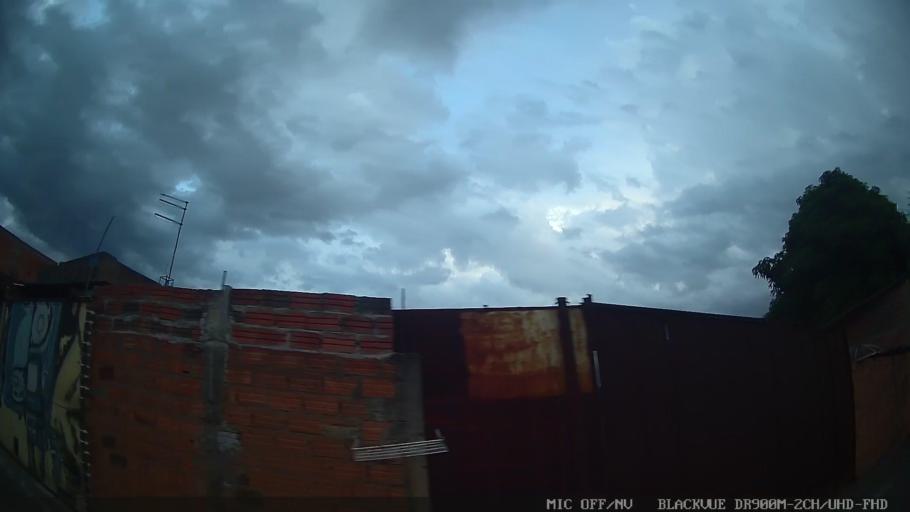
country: BR
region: Sao Paulo
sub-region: Indaiatuba
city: Indaiatuba
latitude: -23.1306
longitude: -47.2358
